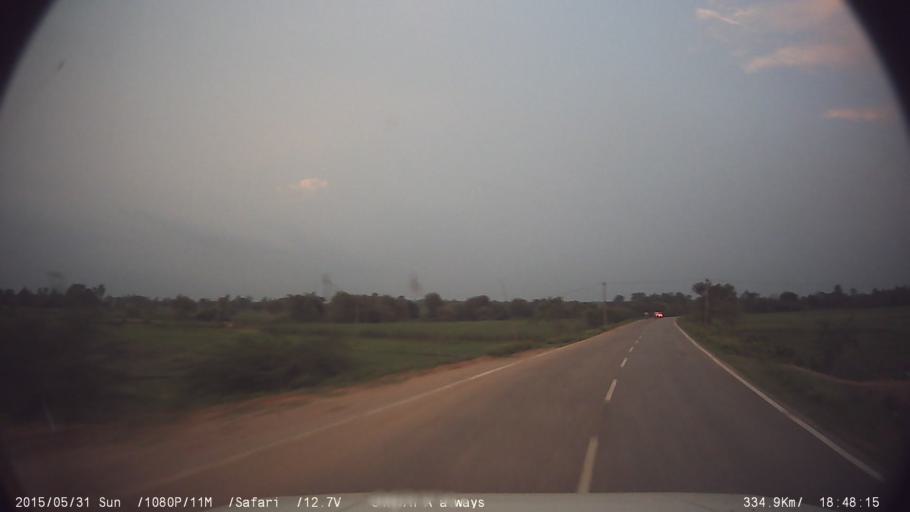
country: IN
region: Karnataka
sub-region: Mysore
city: Tirumakudal Narsipur
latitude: 12.1694
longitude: 76.8415
